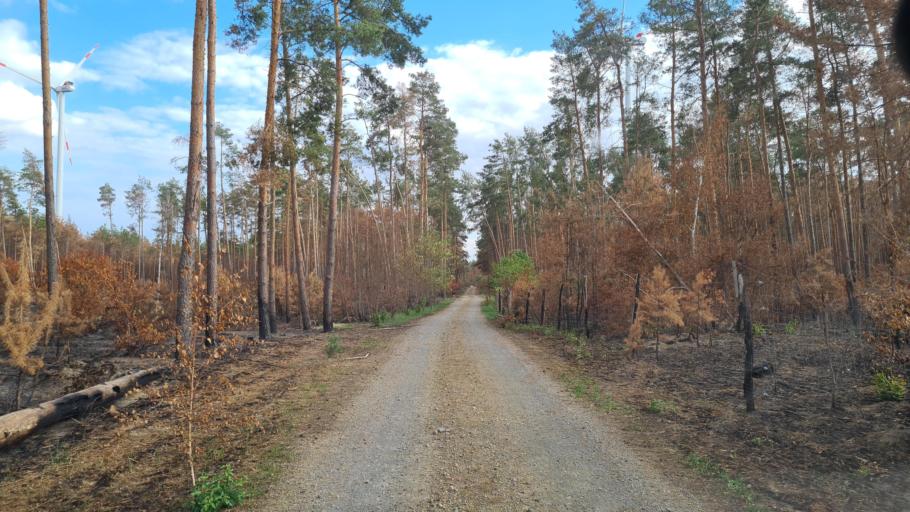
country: DE
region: Saxony
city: Arzberg
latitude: 51.5624
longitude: 13.1832
